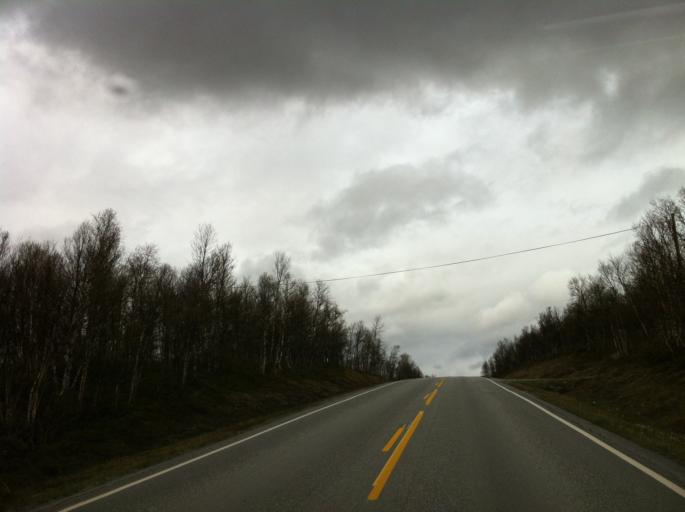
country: NO
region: Sor-Trondelag
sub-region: Roros
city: Roros
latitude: 62.6153
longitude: 11.8460
